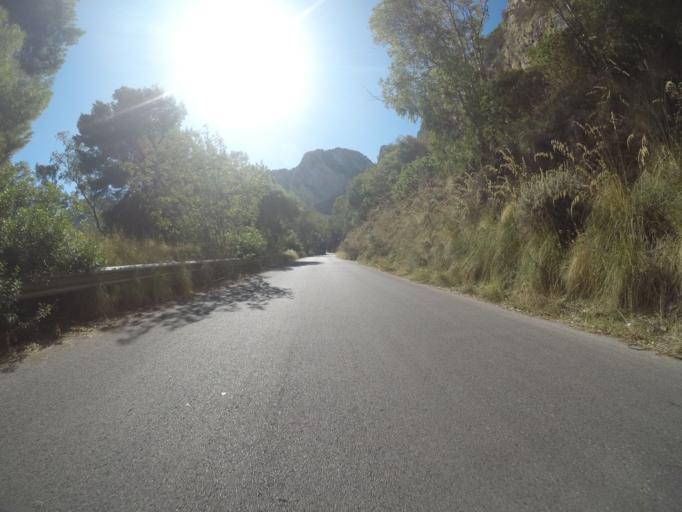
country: IT
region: Sicily
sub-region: Palermo
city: Palermo
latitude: 38.1913
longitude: 13.3393
